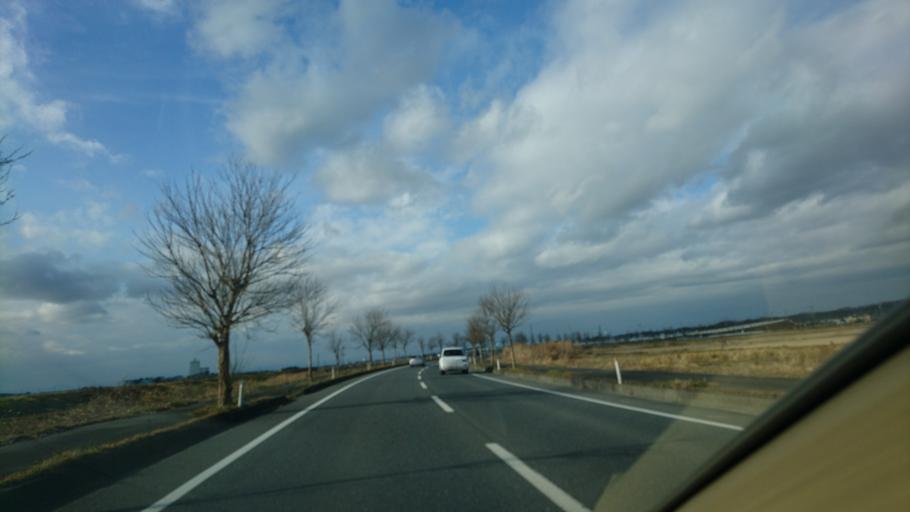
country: JP
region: Miyagi
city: Wakuya
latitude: 38.5407
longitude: 141.1105
